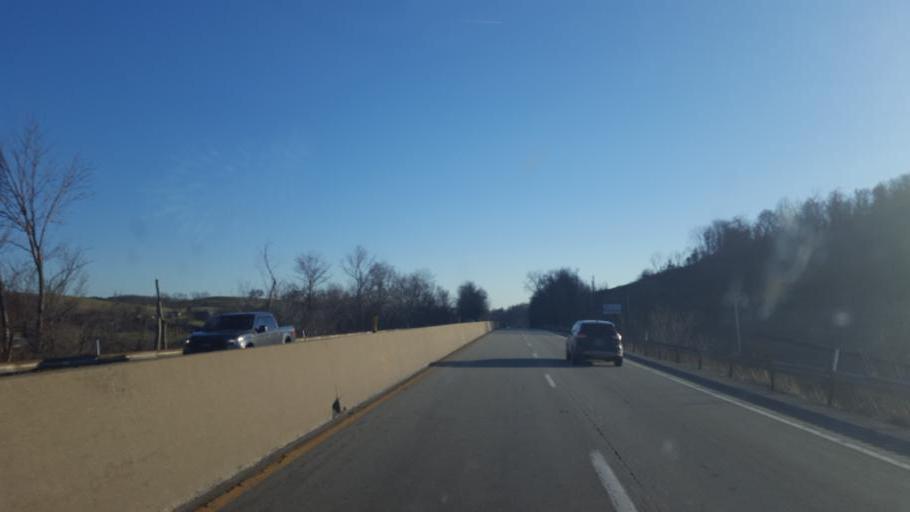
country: US
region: Pennsylvania
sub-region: Westmoreland County
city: West Newton
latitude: 40.1824
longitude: -79.7105
